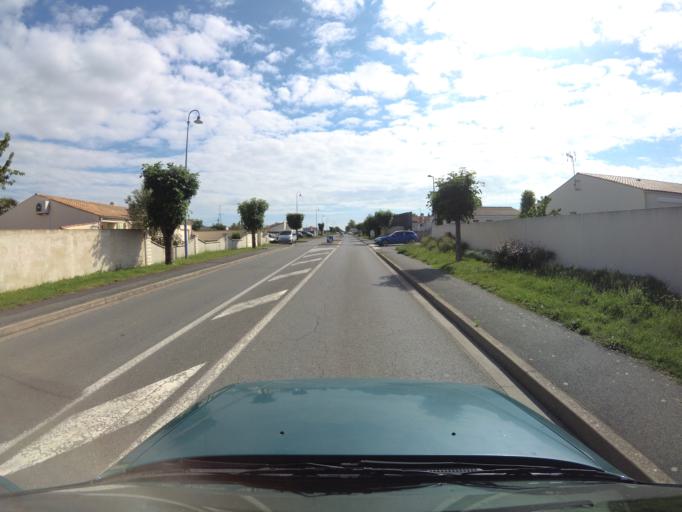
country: FR
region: Poitou-Charentes
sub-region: Departement de la Charente-Maritime
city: Saint-Xandre
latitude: 46.2377
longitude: -1.0704
